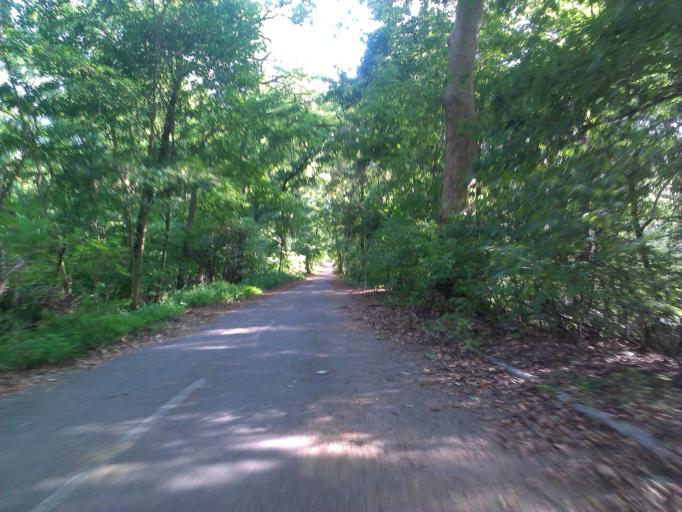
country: DE
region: Baden-Wuerttemberg
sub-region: Karlsruhe Region
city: Ilvesheim
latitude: 49.4418
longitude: 8.5594
